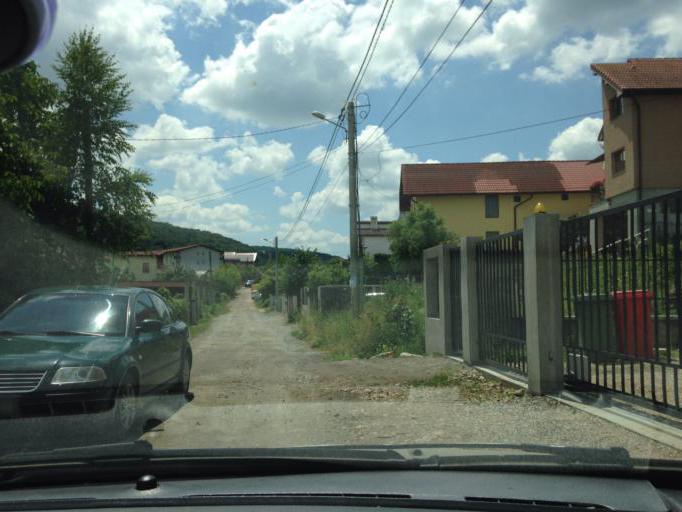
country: RO
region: Cluj
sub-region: Comuna Floresti
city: Floresti
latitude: 46.7441
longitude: 23.5319
